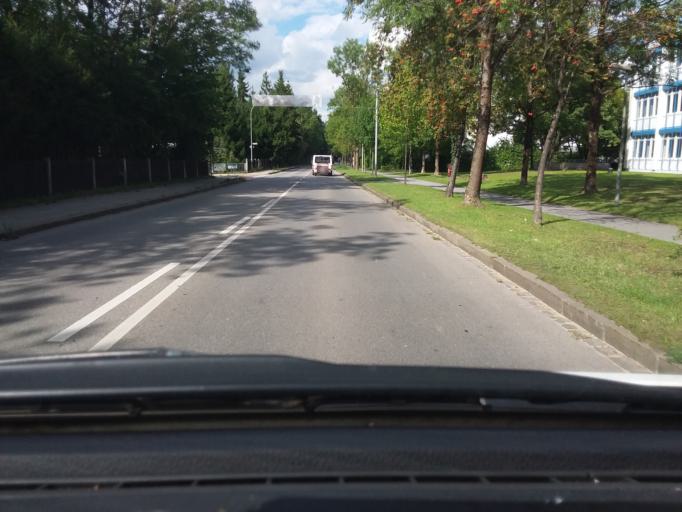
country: DE
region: Bavaria
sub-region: Upper Bavaria
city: Ismaning
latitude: 48.2342
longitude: 11.6778
